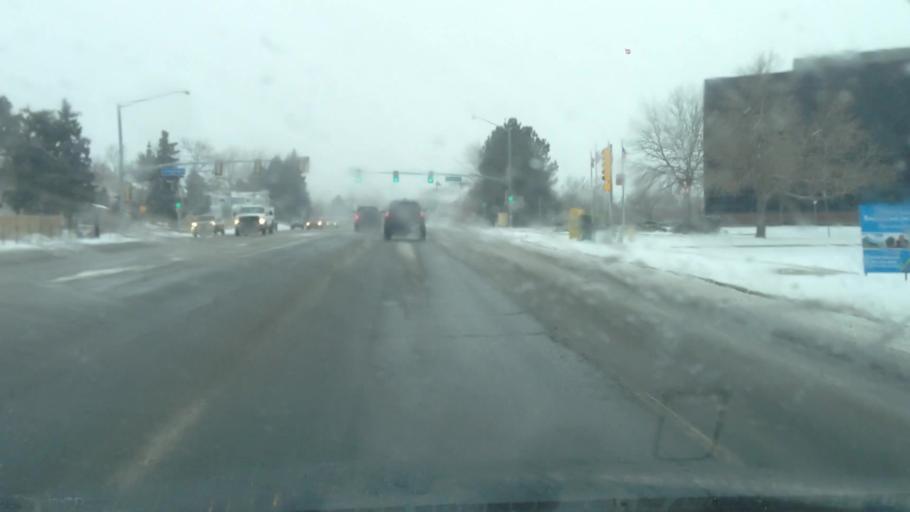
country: US
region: Colorado
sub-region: Adams County
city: Aurora
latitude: 39.6638
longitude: -104.8588
